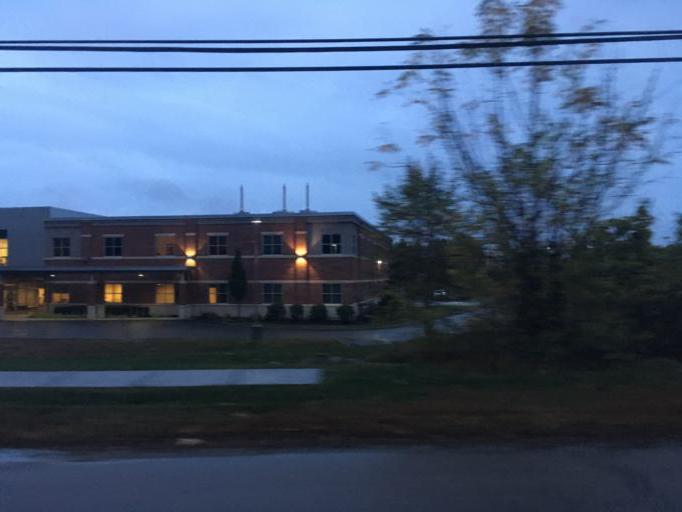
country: US
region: Rhode Island
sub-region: Kent County
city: East Greenwich
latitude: 41.6571
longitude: -71.4973
